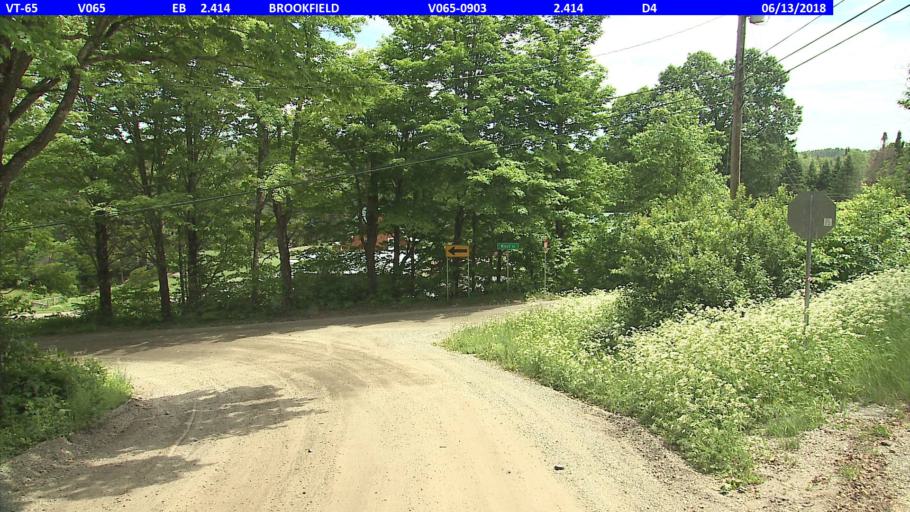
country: US
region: Vermont
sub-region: Orange County
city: Williamstown
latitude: 44.0433
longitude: -72.6146
